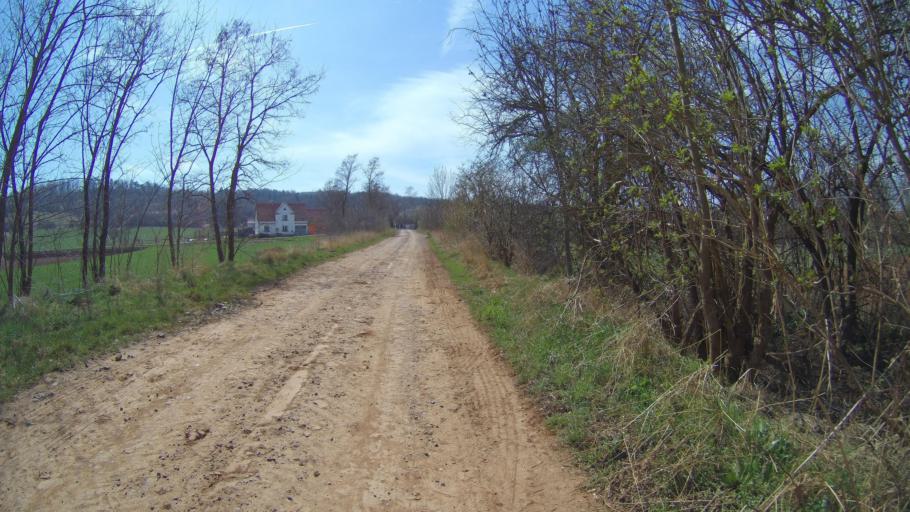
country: CZ
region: Ustecky
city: Podborany
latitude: 50.2189
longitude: 13.4761
